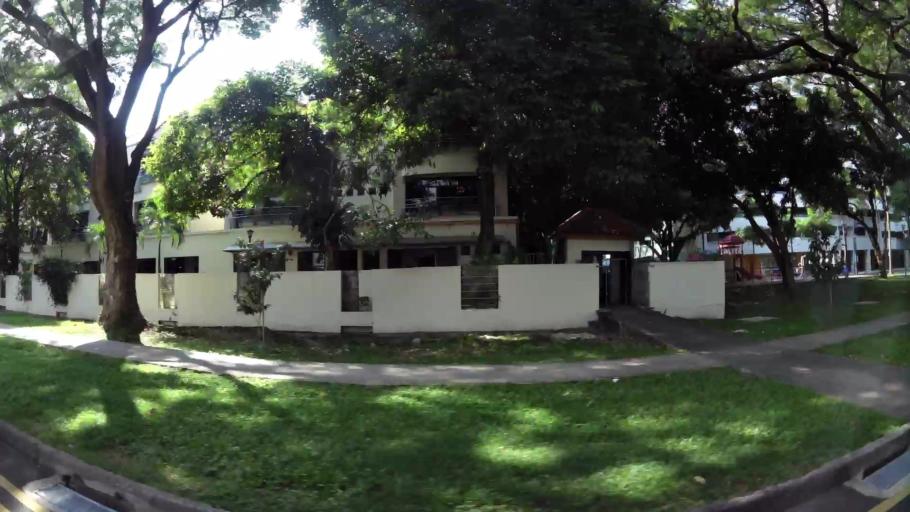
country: SG
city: Singapore
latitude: 1.3191
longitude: 103.8880
